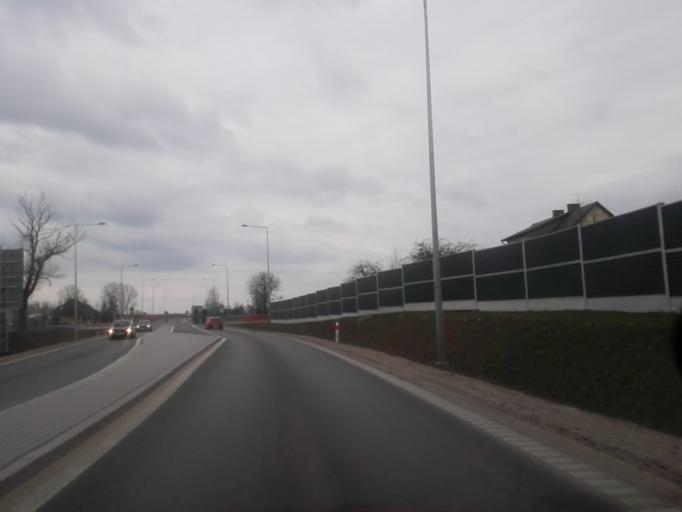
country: PL
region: Podlasie
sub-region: Powiat augustowski
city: Augustow
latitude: 53.8314
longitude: 22.9576
